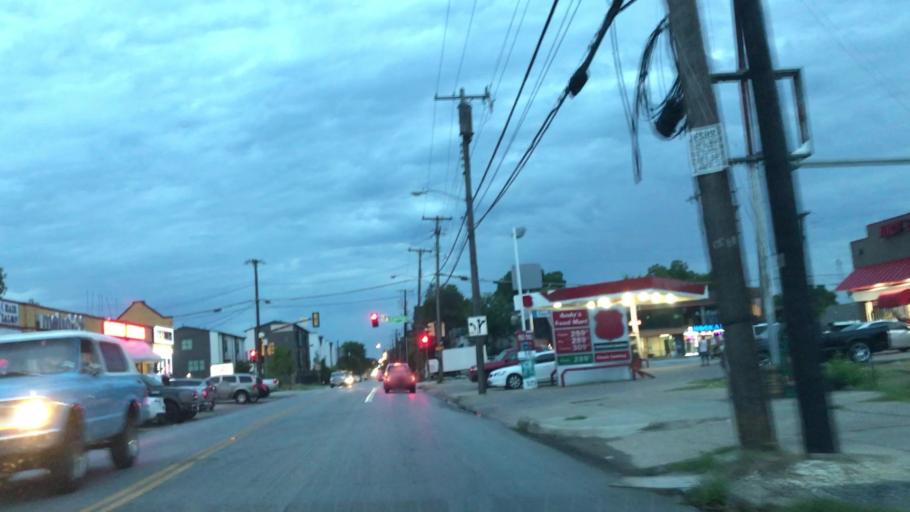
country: US
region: Texas
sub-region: Dallas County
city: Highland Park
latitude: 32.8117
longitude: -96.7827
